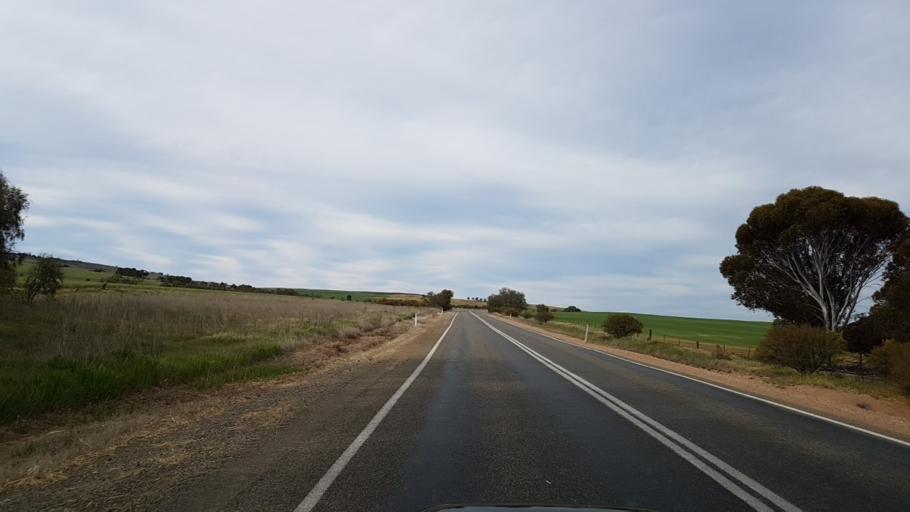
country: AU
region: South Australia
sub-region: Northern Areas
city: Jamestown
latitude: -33.2129
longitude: 138.4220
